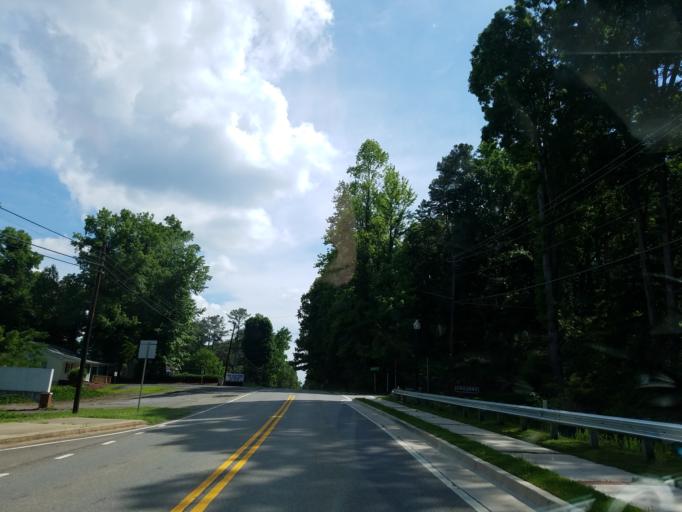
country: US
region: Georgia
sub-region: Cherokee County
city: Holly Springs
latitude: 34.1685
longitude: -84.5048
